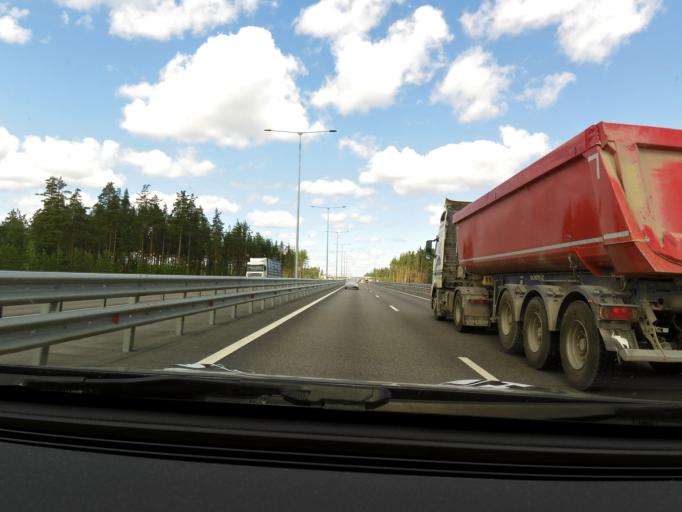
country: RU
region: Tverskaya
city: Krasnomayskiy
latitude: 57.6932
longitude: 34.2114
